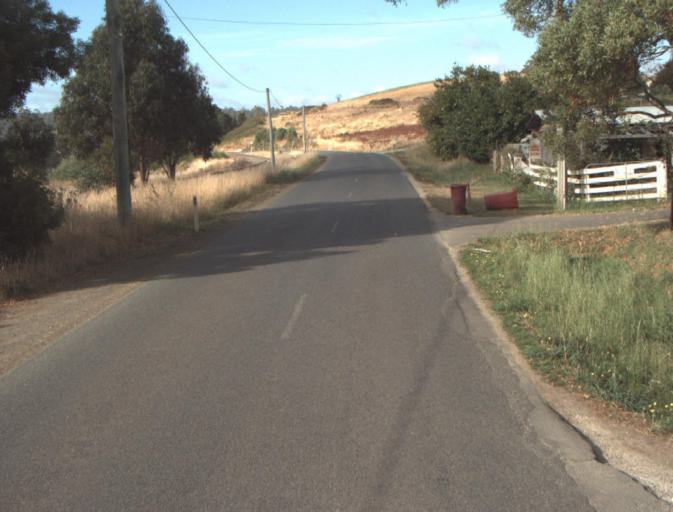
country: AU
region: Tasmania
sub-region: Launceston
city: Mayfield
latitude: -41.1811
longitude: 147.2237
